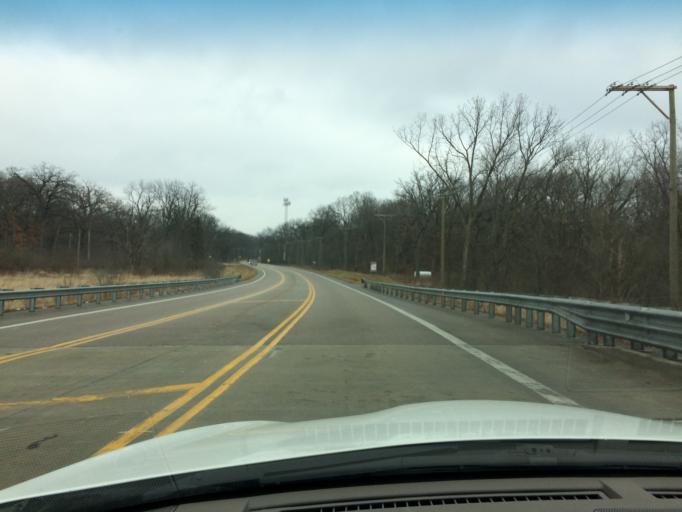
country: US
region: Illinois
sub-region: Kane County
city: Sugar Grove
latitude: 41.7801
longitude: -88.4398
